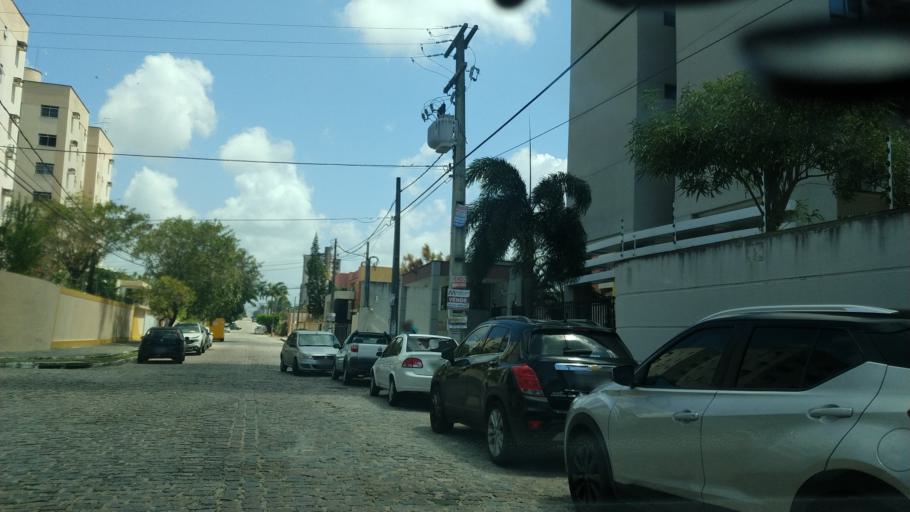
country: BR
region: Rio Grande do Norte
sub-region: Natal
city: Natal
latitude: -5.8623
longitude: -35.1952
